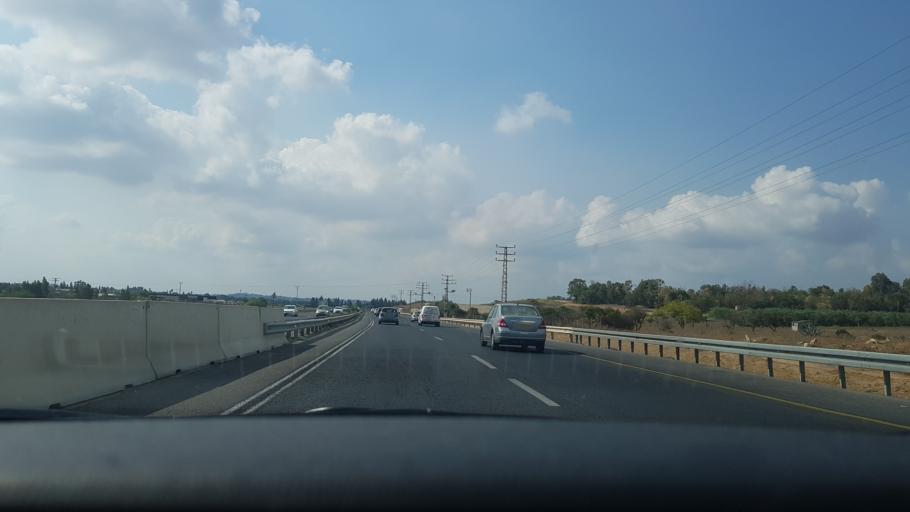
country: IL
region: Central District
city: Mazkeret Batya
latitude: 31.8585
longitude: 34.8055
